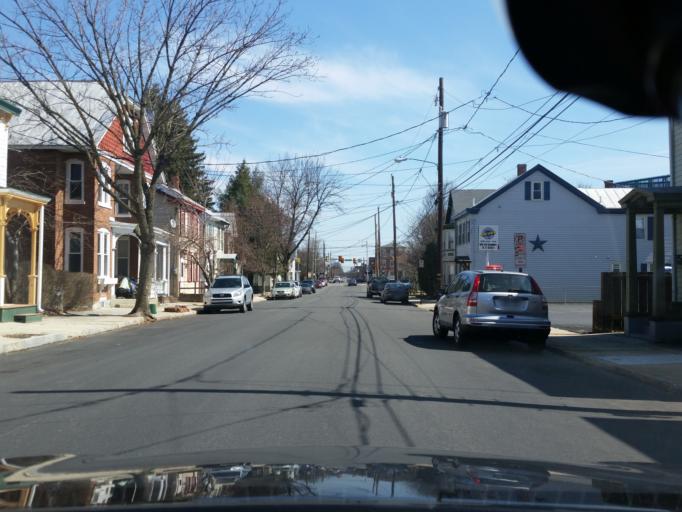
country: US
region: Pennsylvania
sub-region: Cumberland County
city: Carlisle
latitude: 40.2053
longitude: -77.1981
